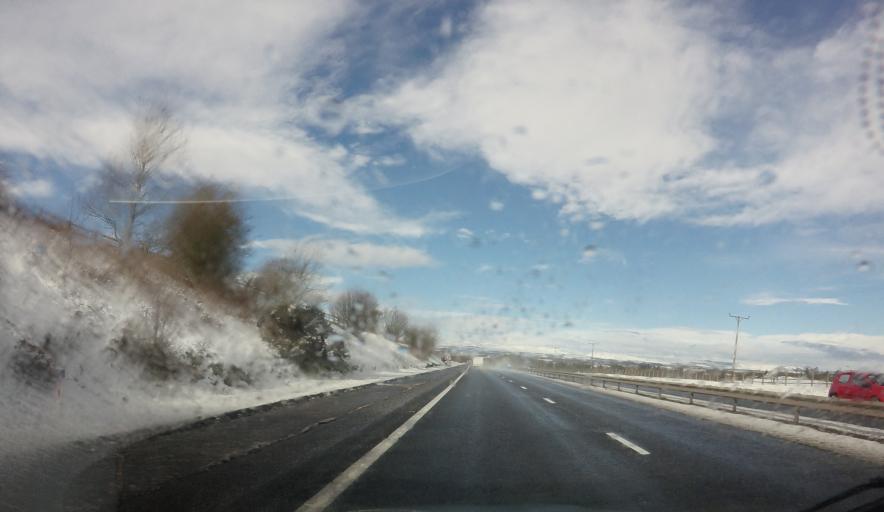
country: GB
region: Scotland
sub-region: Perth and Kinross
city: Perth
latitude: 56.3778
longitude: -3.4518
